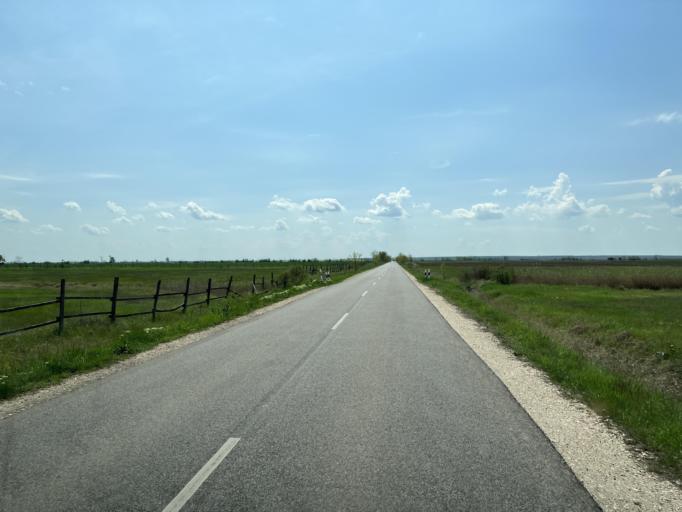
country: HU
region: Pest
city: Tapioszentmarton
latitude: 47.3037
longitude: 19.7586
